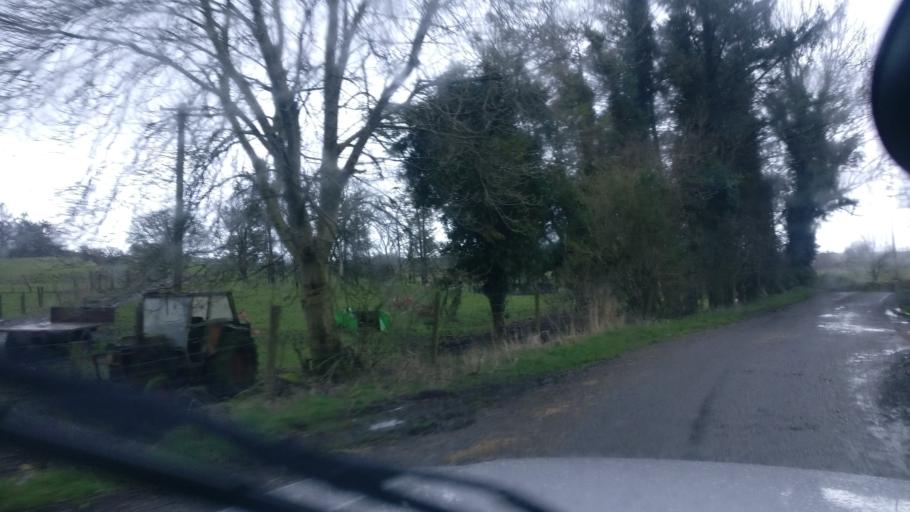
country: IE
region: Connaught
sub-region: County Galway
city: Loughrea
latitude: 53.2470
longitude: -8.4269
